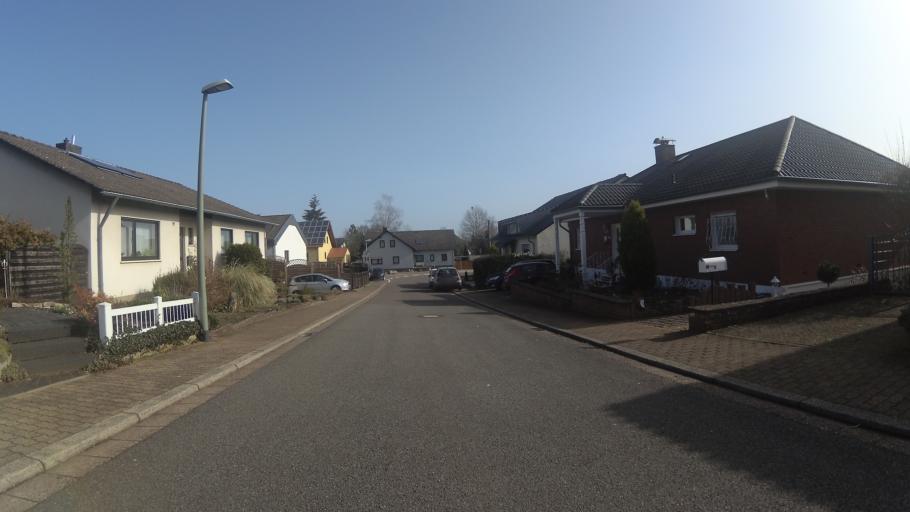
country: DE
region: Saarland
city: Uberherrn
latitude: 49.2740
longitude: 6.6985
